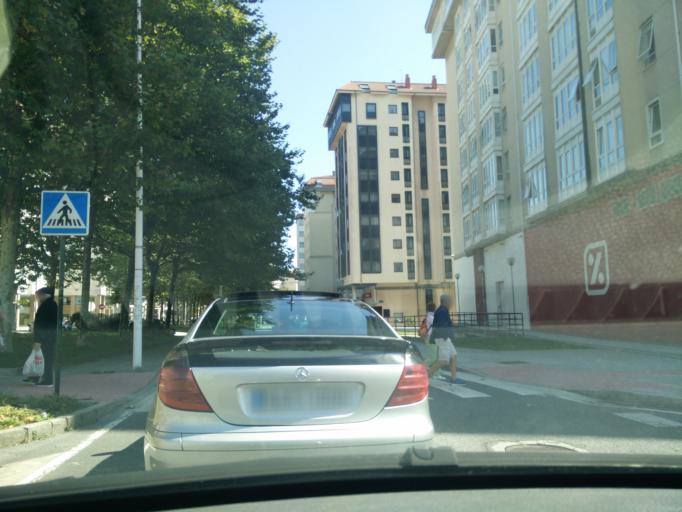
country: ES
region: Galicia
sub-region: Provincia da Coruna
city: A Coruna
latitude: 43.3745
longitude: -8.4317
